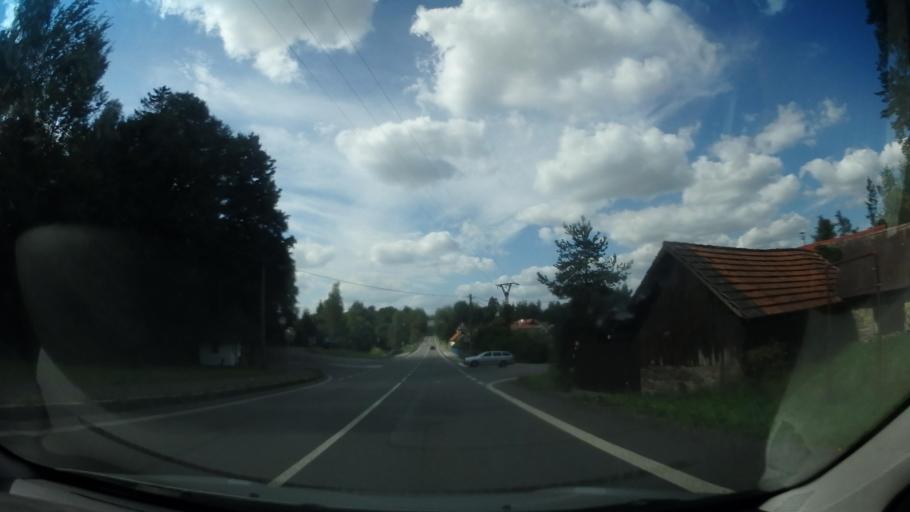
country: CZ
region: Vysocina
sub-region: Okres Zd'ar nad Sazavou
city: Nove Veseli
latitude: 49.5599
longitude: 15.8633
